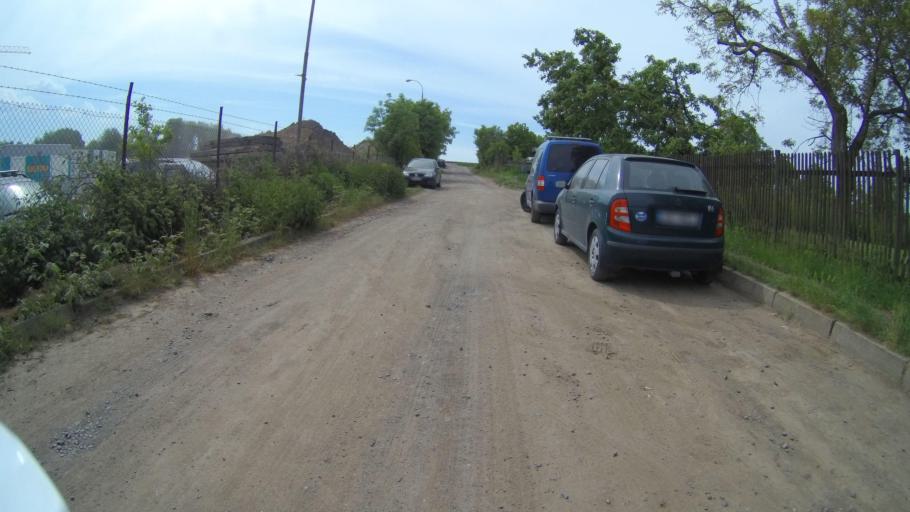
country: CZ
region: Praha
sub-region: Praha 9
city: Strizkov
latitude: 50.1478
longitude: 14.4731
